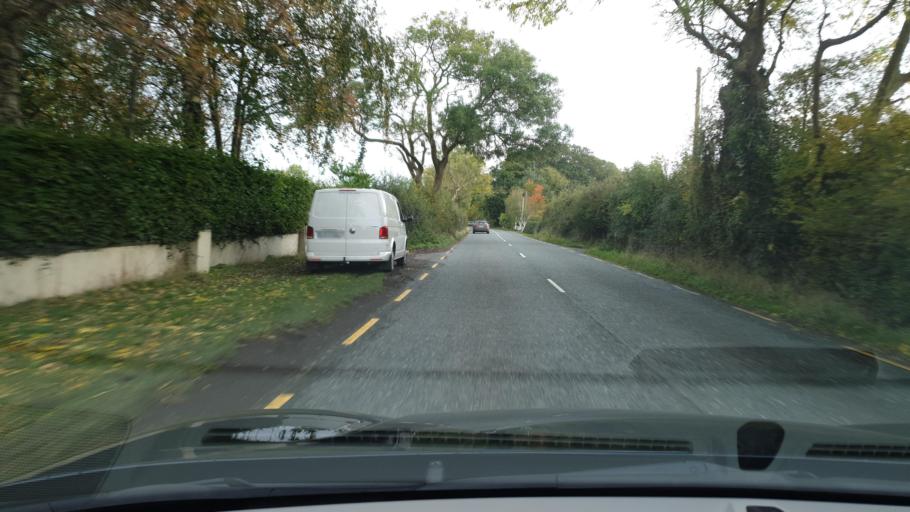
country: IE
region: Leinster
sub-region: An Mhi
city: Ashbourne
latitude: 53.5001
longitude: -6.4283
